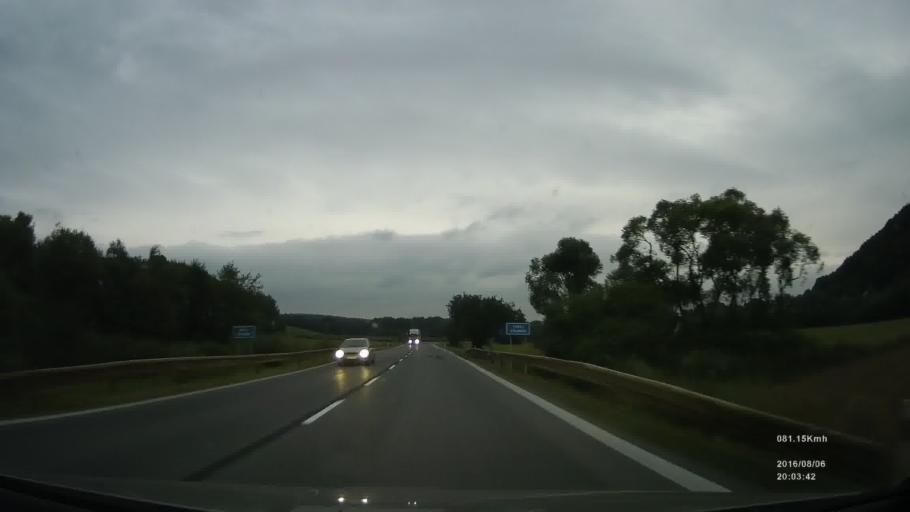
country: SK
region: Presovsky
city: Stropkov
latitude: 49.2469
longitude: 21.6126
